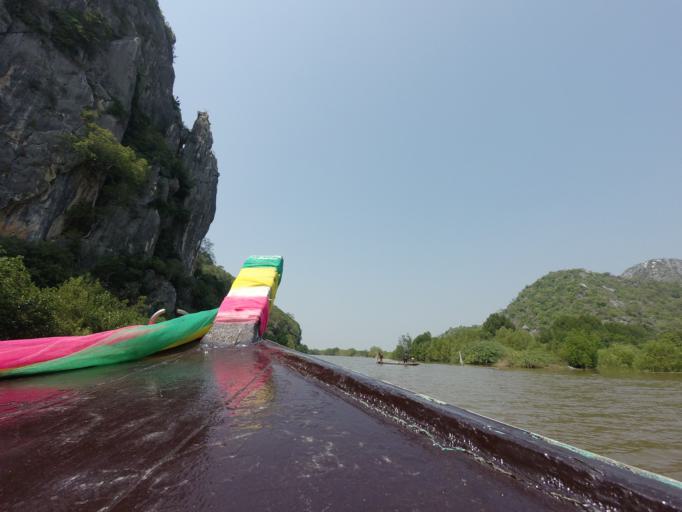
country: TH
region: Prachuap Khiri Khan
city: Kui Buri
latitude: 12.1417
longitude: 99.9560
